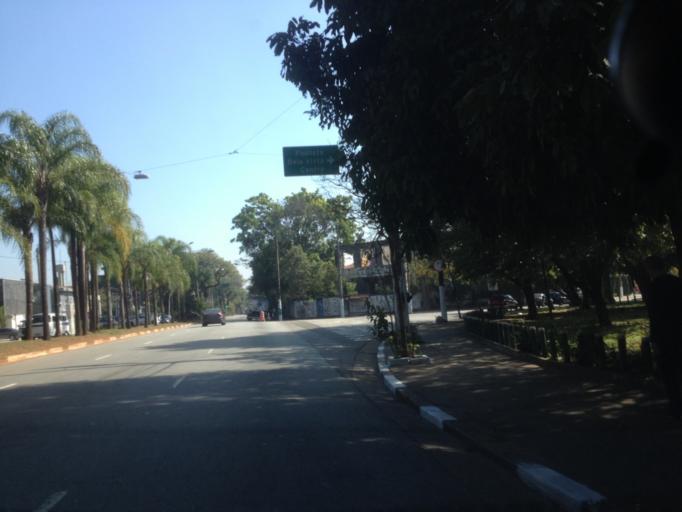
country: BR
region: Sao Paulo
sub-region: Sao Paulo
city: Sao Paulo
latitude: -23.5782
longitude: -46.6626
